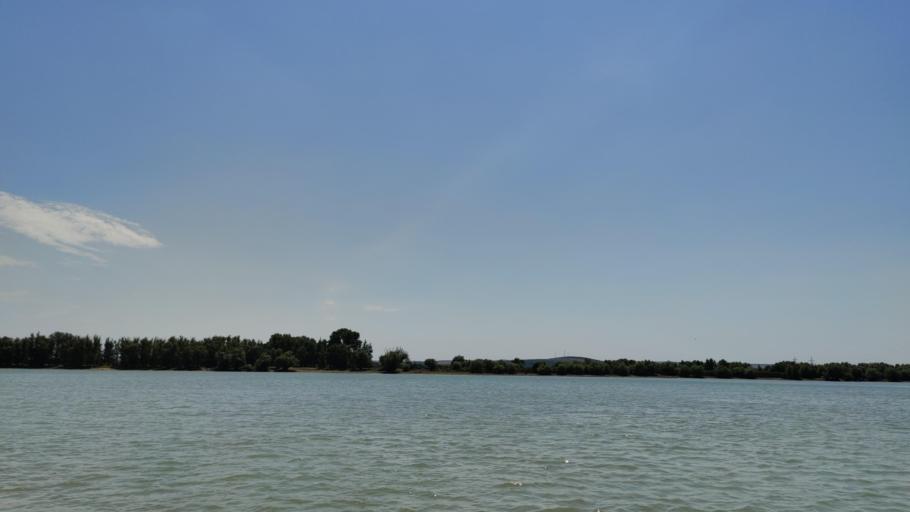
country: RO
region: Tulcea
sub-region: Municipiul Tulcea
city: Tulcea
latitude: 45.2046
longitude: 28.8526
